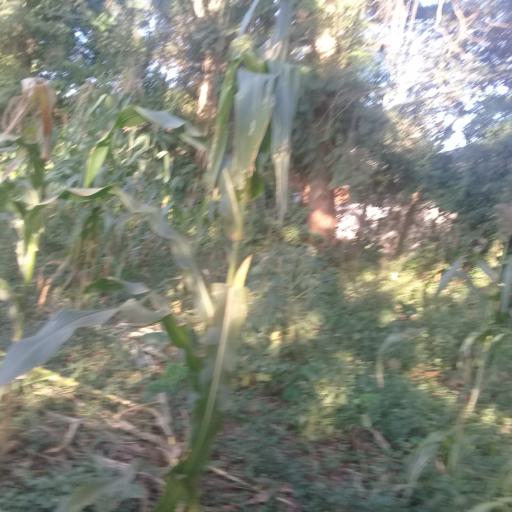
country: UG
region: Central Region
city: Kampala Central Division
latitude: 0.3375
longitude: 32.5649
